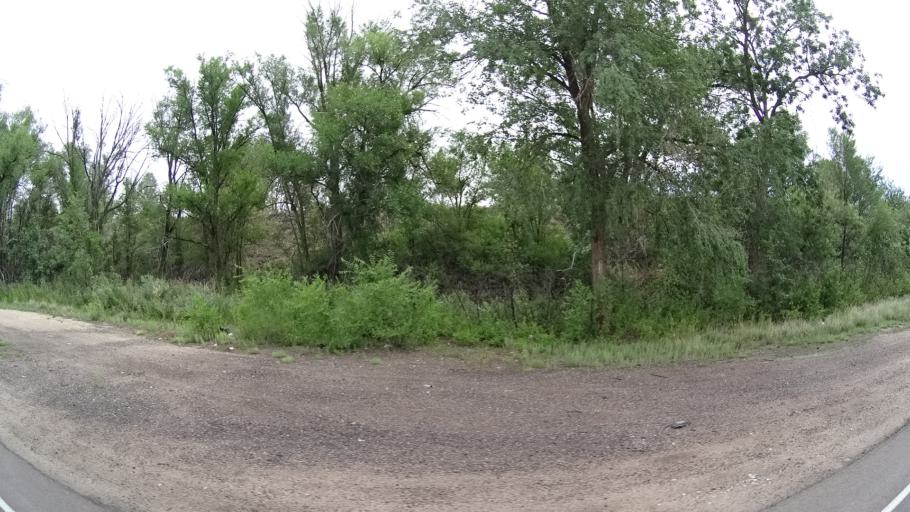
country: US
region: Colorado
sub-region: El Paso County
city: Fountain
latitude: 38.7045
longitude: -104.7097
